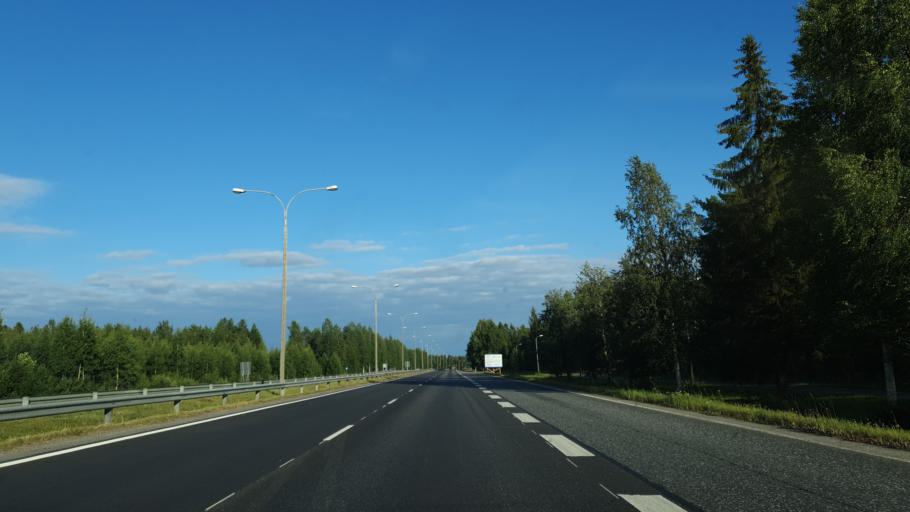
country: FI
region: North Karelia
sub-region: Joensuu
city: Joensuu
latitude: 62.6267
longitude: 29.7044
